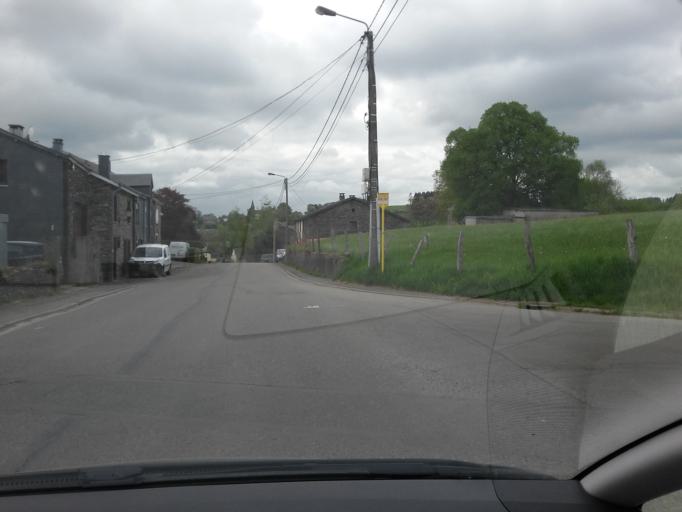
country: BE
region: Wallonia
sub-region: Province du Luxembourg
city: Bertrix
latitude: 49.8233
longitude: 5.3229
